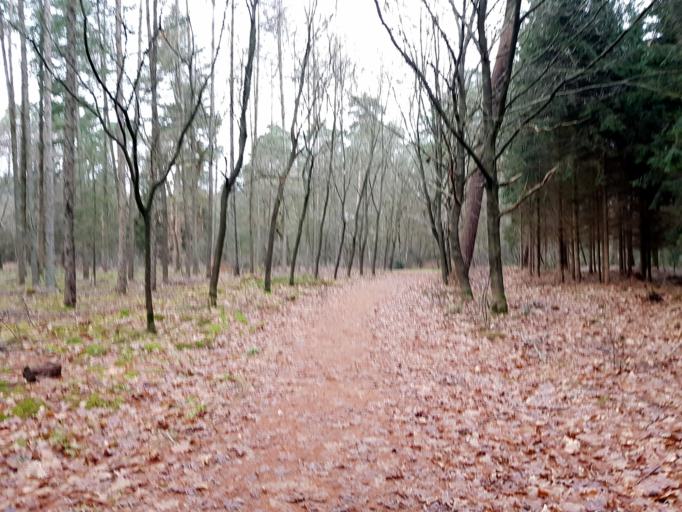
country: NL
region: Utrecht
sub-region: Gemeente Utrechtse Heuvelrug
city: Maarn
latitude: 52.0539
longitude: 5.3668
